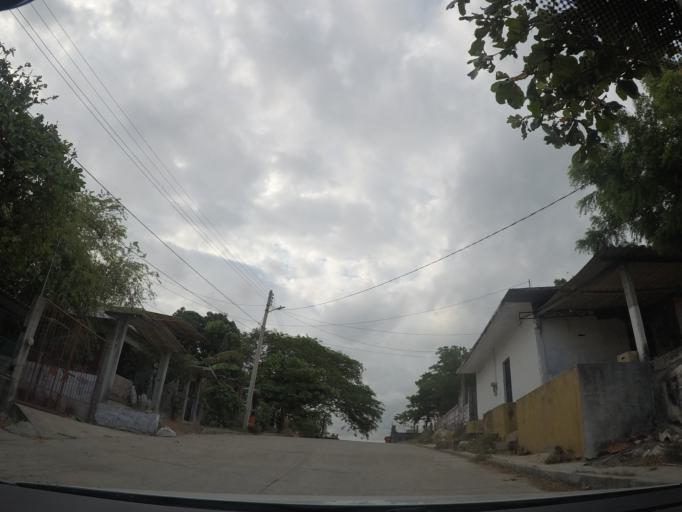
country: MX
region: Oaxaca
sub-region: Salina Cruz
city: Salina Cruz
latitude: 16.2123
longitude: -95.1977
